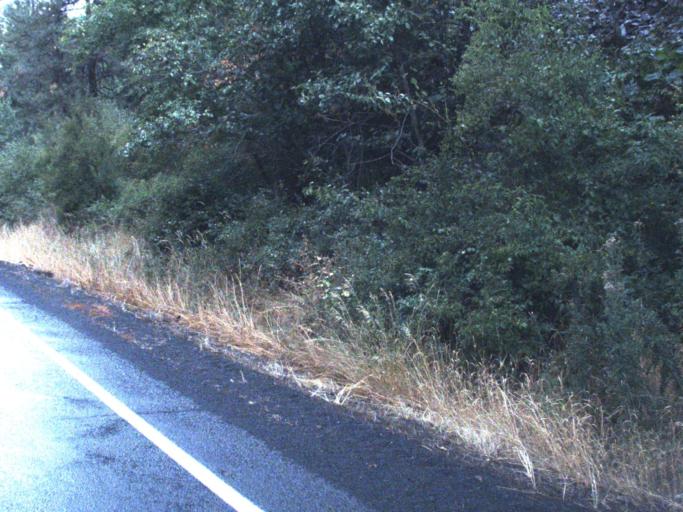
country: US
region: Washington
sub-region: Lincoln County
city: Davenport
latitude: 47.7584
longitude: -117.8910
